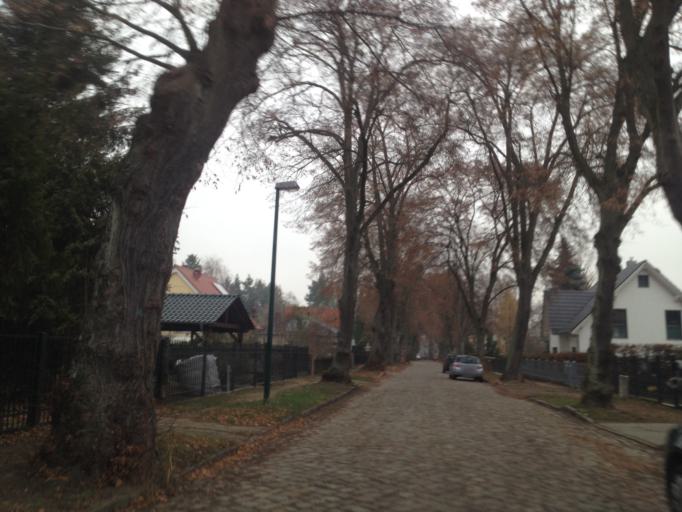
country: DE
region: Berlin
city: Blankenfelde
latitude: 52.6880
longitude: 13.3741
